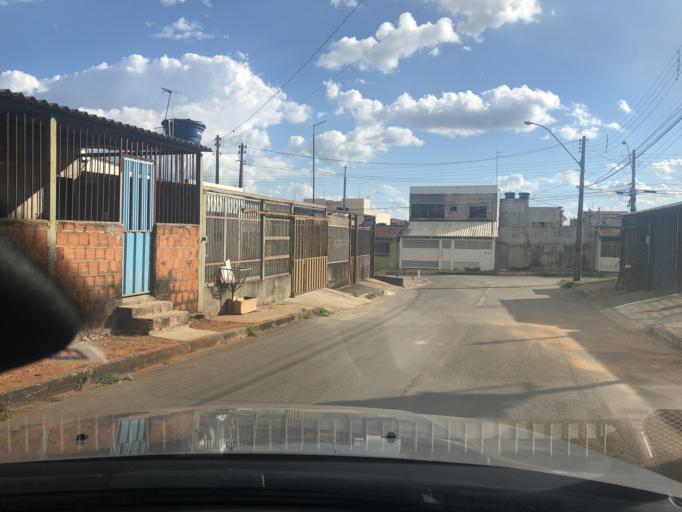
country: BR
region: Federal District
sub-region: Brasilia
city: Brasilia
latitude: -15.9205
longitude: -48.0569
